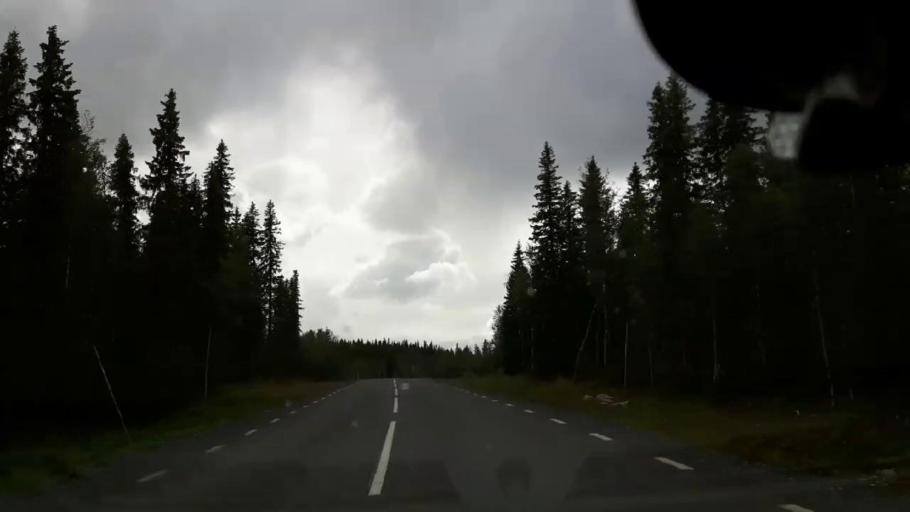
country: SE
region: Jaemtland
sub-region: Krokoms Kommun
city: Valla
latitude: 63.4410
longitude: 13.8241
